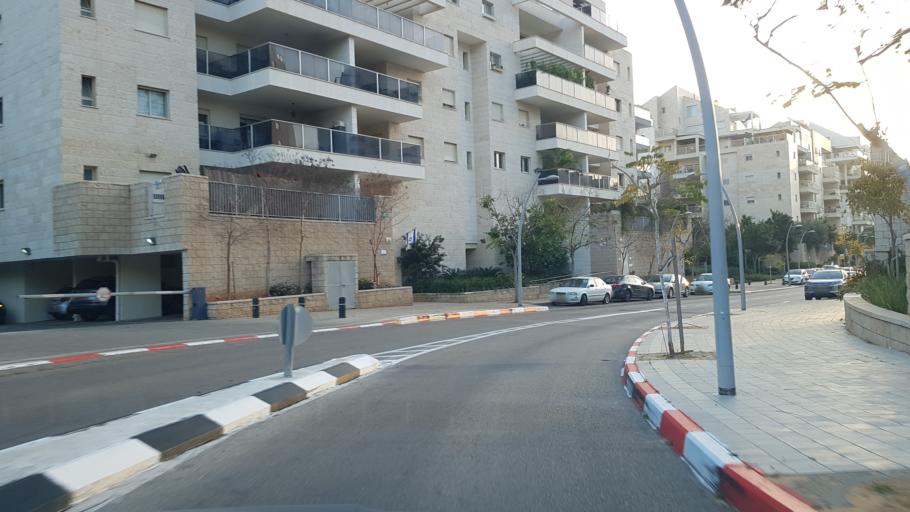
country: IL
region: Central District
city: Kfar Saba
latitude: 32.1951
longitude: 34.8969
